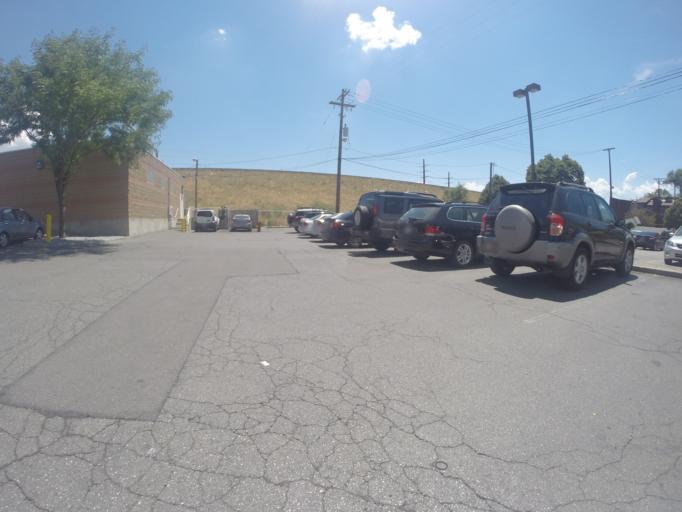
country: US
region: Utah
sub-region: Salt Lake County
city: Willard
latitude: 40.7204
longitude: -111.8585
